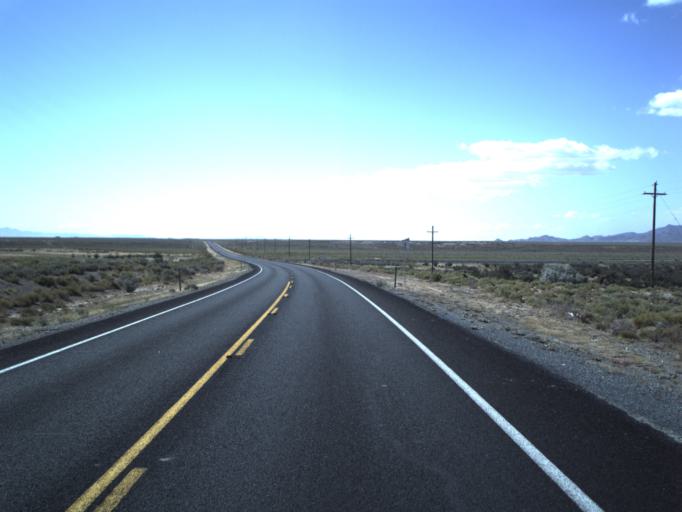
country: US
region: Utah
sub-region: Beaver County
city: Milford
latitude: 38.4595
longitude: -113.0043
